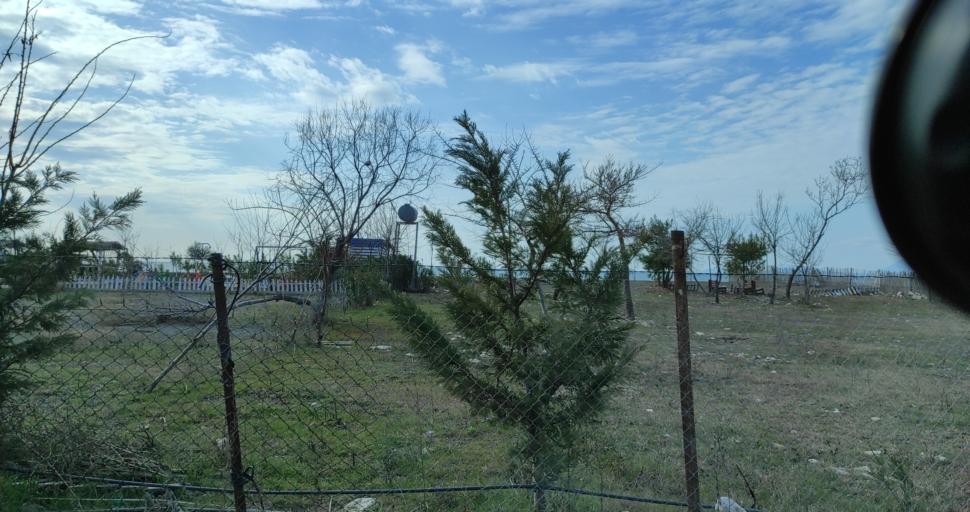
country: AL
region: Lezhe
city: Shengjin
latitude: 41.7736
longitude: 19.6025
